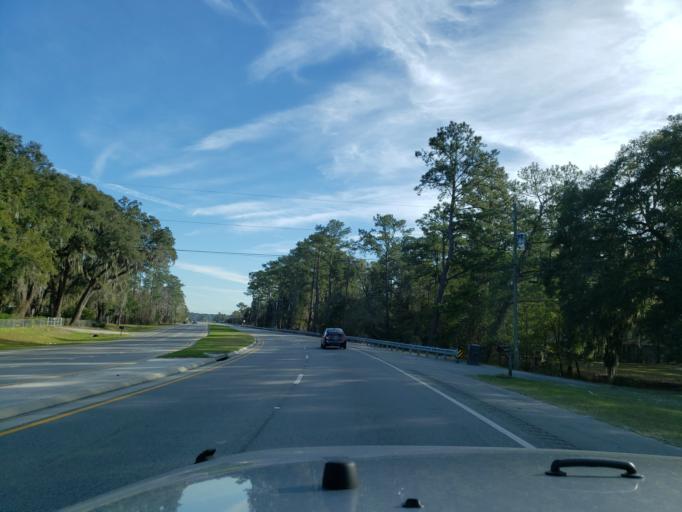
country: US
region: Georgia
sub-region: Chatham County
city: Georgetown
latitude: 32.0465
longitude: -81.2144
